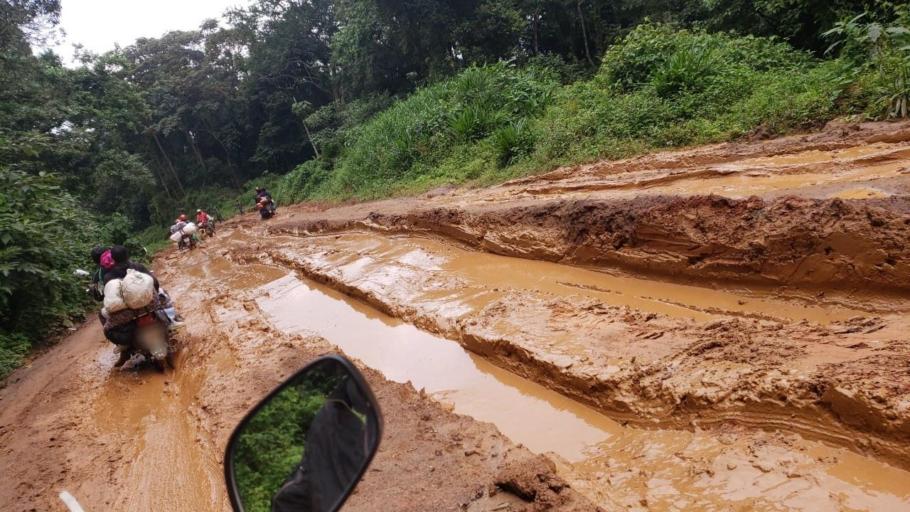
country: CD
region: South Kivu
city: Kabare
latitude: -2.2526
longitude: 28.6461
